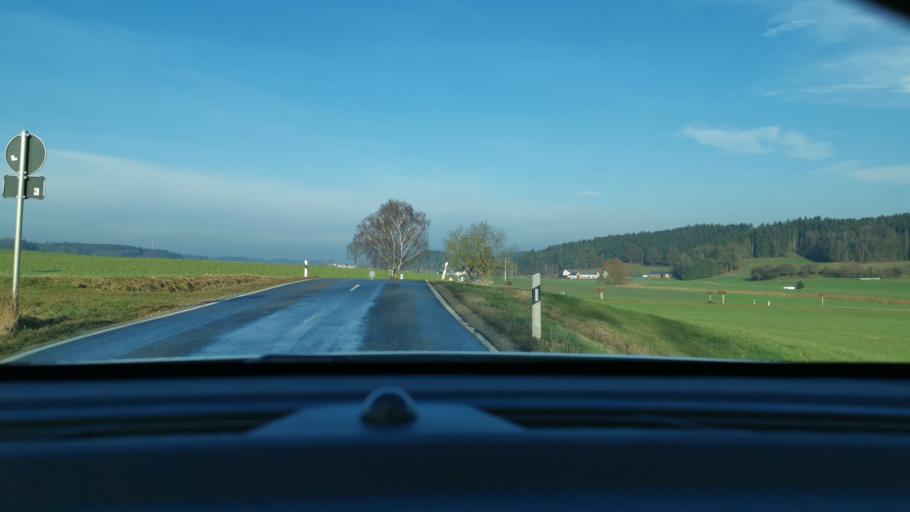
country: DE
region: Bavaria
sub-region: Swabia
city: Aindling
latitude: 48.5650
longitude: 10.9804
